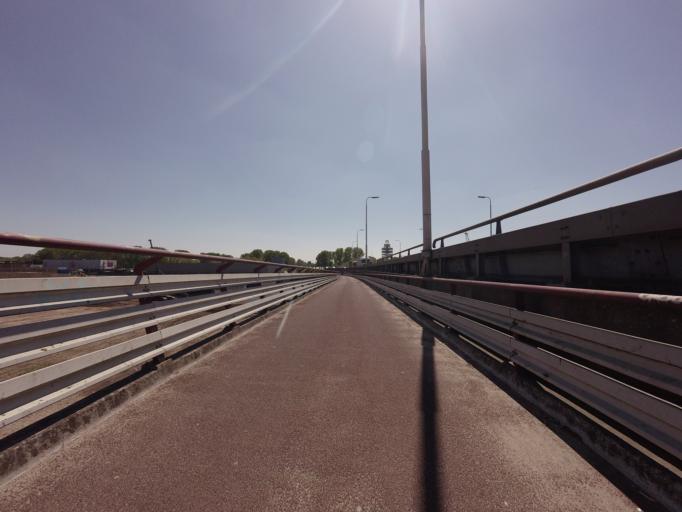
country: NL
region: South Holland
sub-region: Gemeente Papendrecht
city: Papendrecht
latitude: 51.8201
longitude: 4.7064
